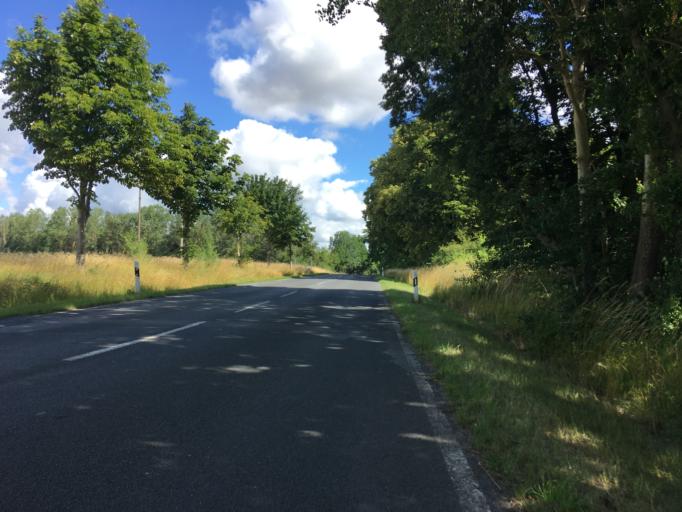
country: DE
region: Brandenburg
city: Mittenwalde
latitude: 53.1891
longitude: 13.5904
